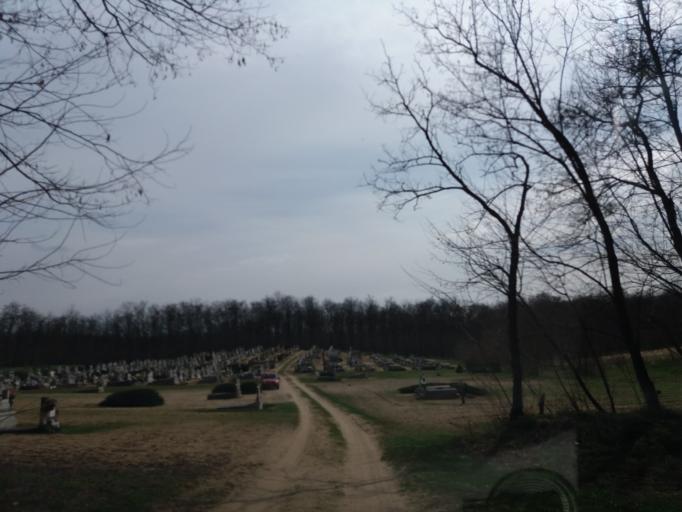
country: HU
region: Szabolcs-Szatmar-Bereg
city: Petnehaza
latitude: 48.0514
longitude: 22.0451
